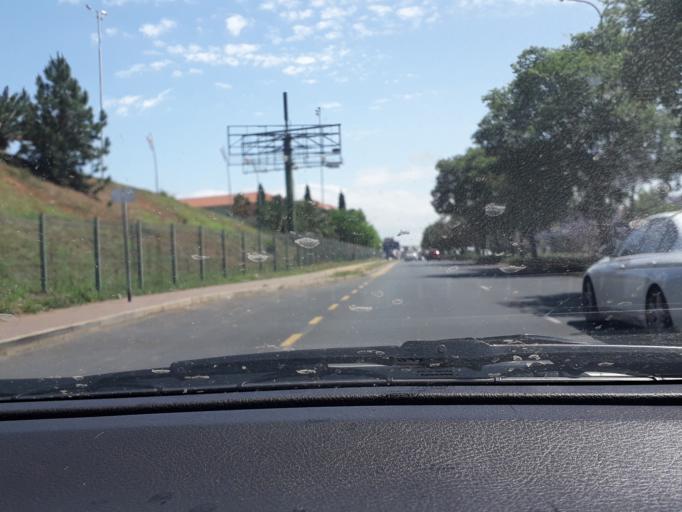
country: ZA
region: Gauteng
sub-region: City of Johannesburg Metropolitan Municipality
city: Midrand
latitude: -26.0638
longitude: 28.0605
